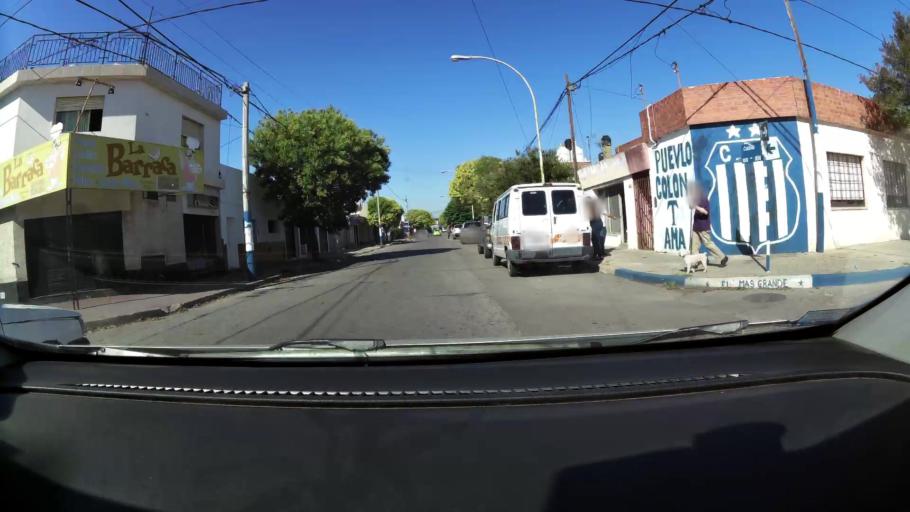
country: AR
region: Cordoba
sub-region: Departamento de Capital
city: Cordoba
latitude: -31.4384
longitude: -64.1597
